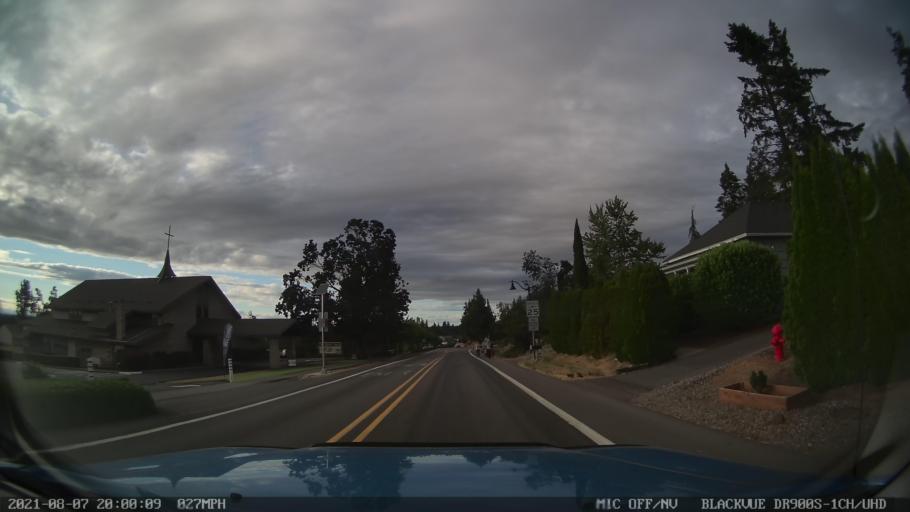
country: US
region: Oregon
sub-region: Marion County
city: Silverton
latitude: 45.0019
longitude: -122.7923
